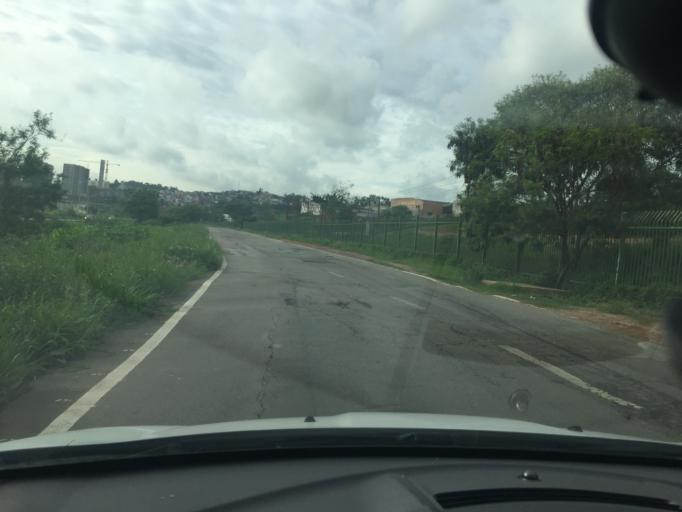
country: BR
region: Sao Paulo
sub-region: Varzea Paulista
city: Varzea Paulista
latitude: -23.2055
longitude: -46.8123
